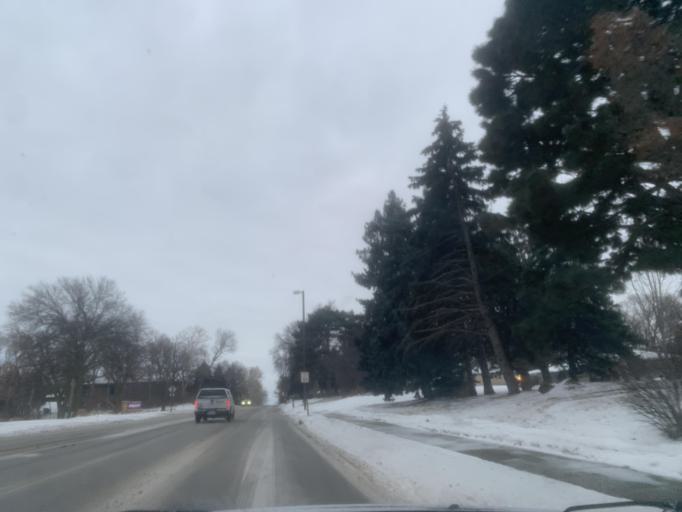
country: US
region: Nebraska
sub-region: Douglas County
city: Ralston
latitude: 41.2610
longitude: -96.0526
